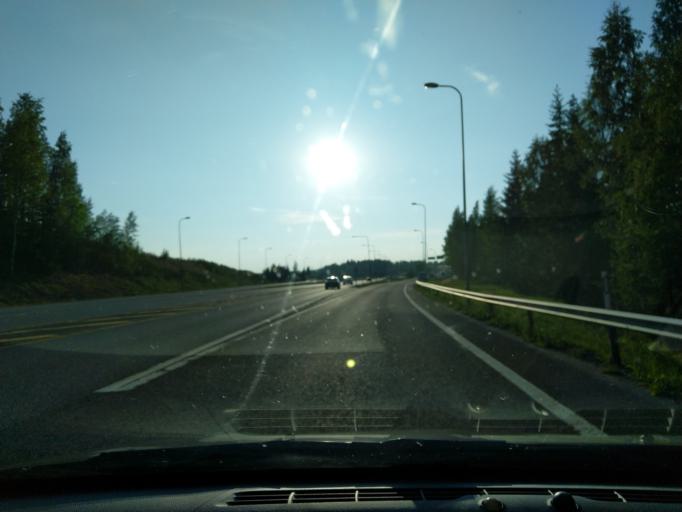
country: FI
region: Paijanne Tavastia
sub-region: Lahti
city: Lahti
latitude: 60.9681
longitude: 25.7312
